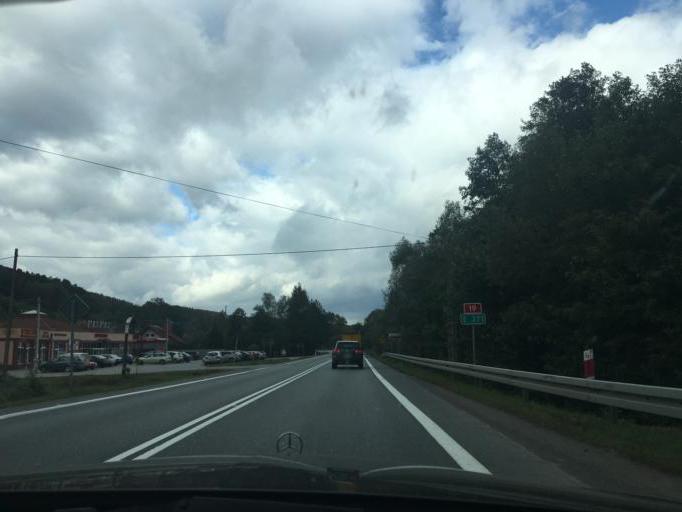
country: PL
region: Subcarpathian Voivodeship
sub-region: Powiat strzyzowski
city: Niebylec
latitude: 49.8603
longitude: 21.9034
